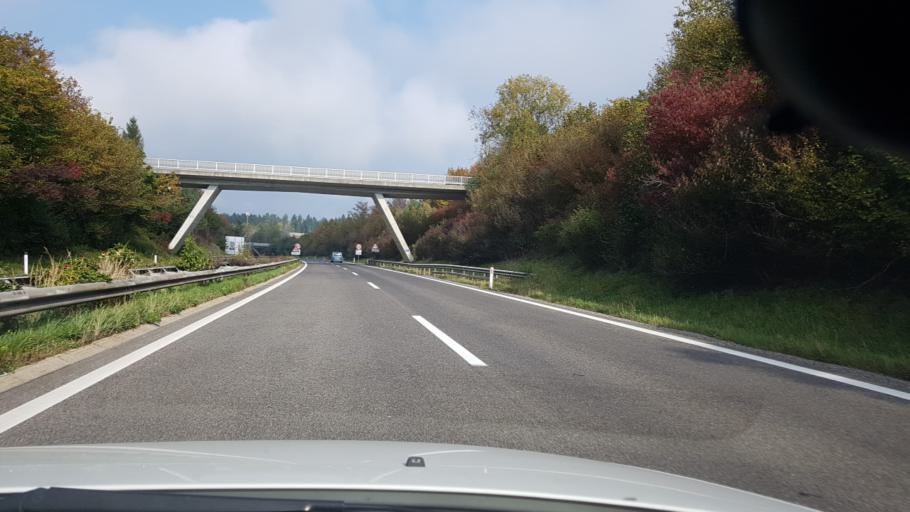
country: AT
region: Carinthia
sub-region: Politischer Bezirk Villach Land
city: Rosegg
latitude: 46.5696
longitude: 14.0062
